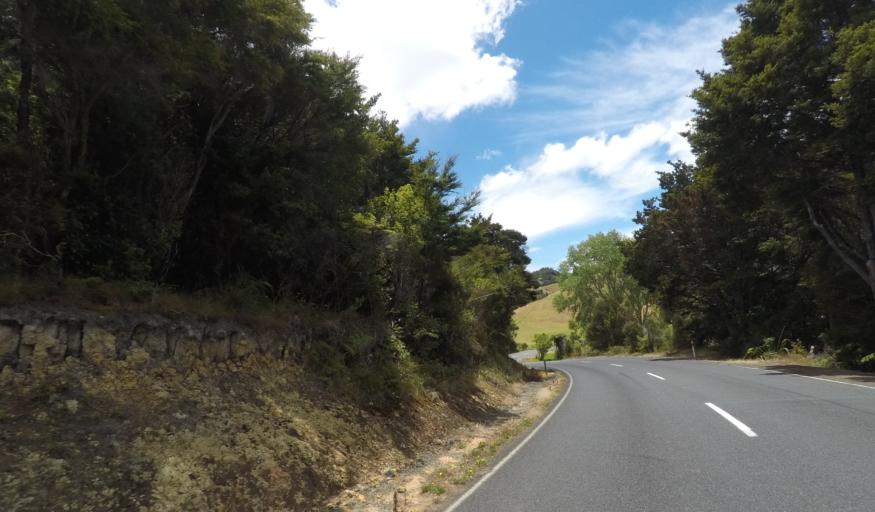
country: NZ
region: Northland
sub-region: Whangarei
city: Ngunguru
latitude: -35.5069
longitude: 174.4394
